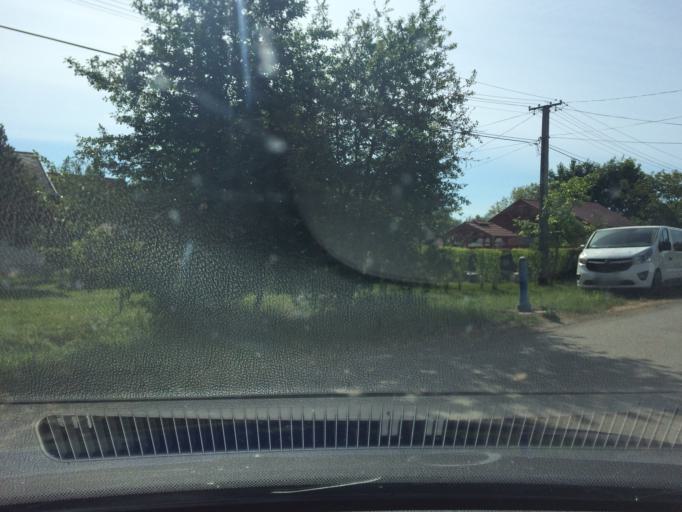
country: HU
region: Szabolcs-Szatmar-Bereg
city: Tiszavasvari
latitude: 47.9545
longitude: 21.3484
